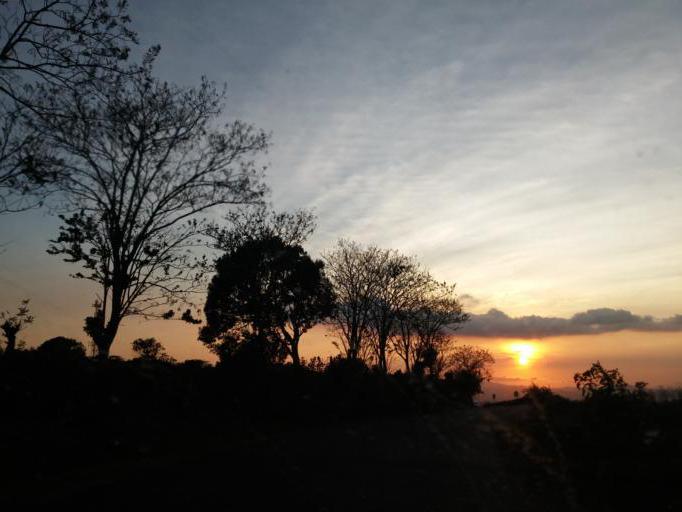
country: CR
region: Alajuela
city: Sabanilla
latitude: 10.0771
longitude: -84.2135
